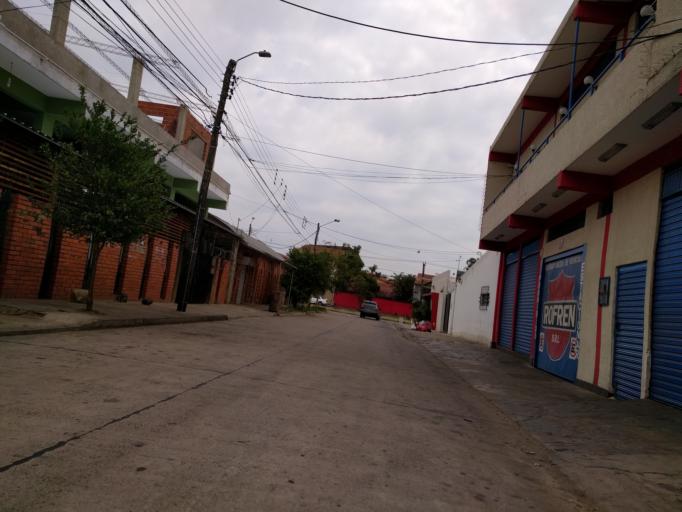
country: BO
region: Santa Cruz
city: Santa Cruz de la Sierra
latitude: -17.7911
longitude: -63.2081
